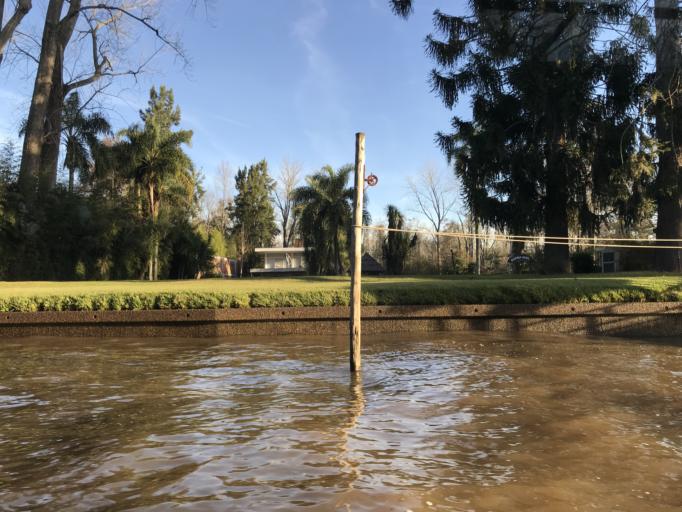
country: AR
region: Buenos Aires
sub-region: Partido de Tigre
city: Tigre
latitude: -34.3722
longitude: -58.5820
